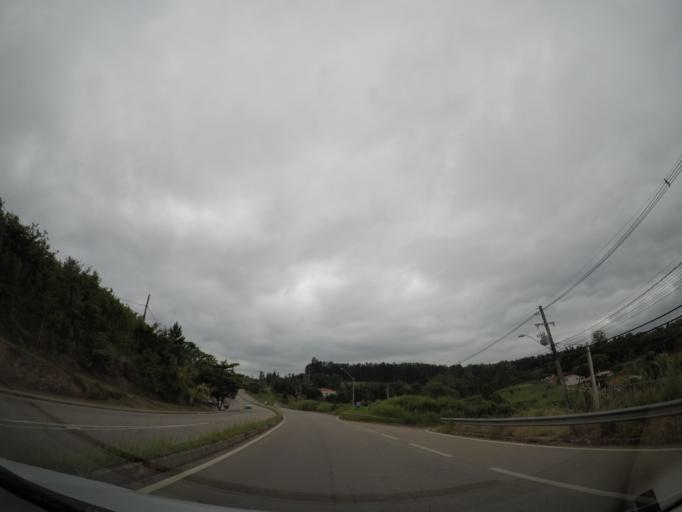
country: BR
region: Sao Paulo
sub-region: Louveira
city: Louveira
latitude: -23.1247
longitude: -46.9327
